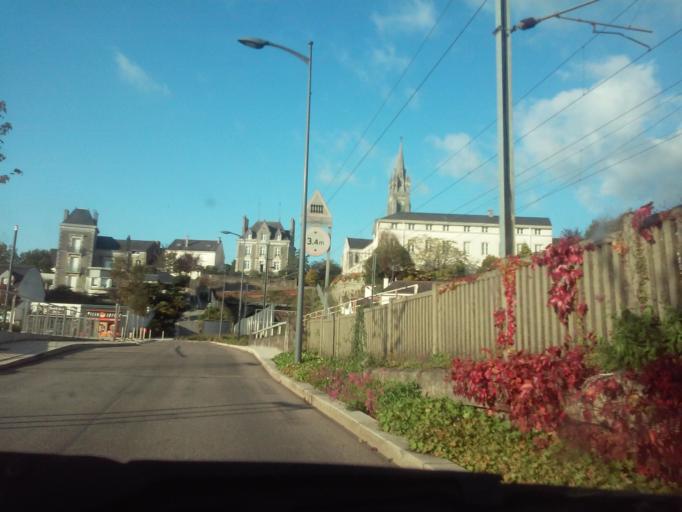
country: FR
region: Pays de la Loire
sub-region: Departement de la Loire-Atlantique
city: Pontchateau
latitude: 47.4362
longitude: -2.0885
